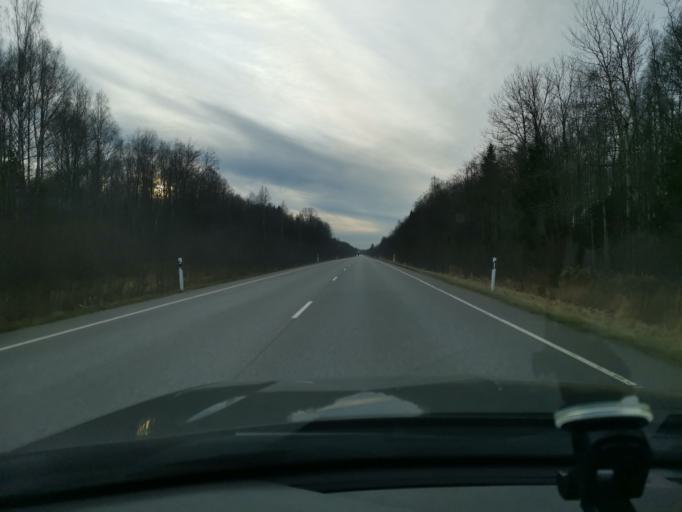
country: EE
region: Ida-Virumaa
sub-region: Narva-Joesuu linn
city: Narva-Joesuu
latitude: 59.3321
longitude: 27.9515
